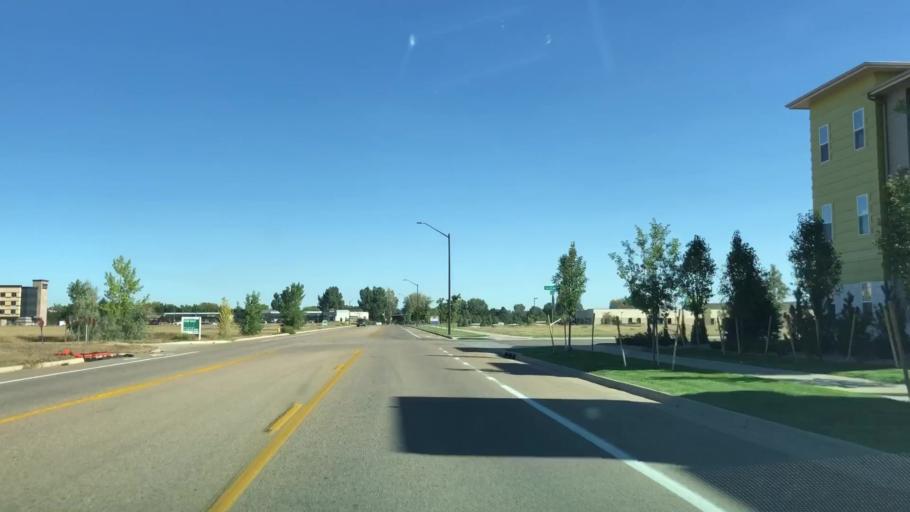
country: US
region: Colorado
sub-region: Larimer County
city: Fort Collins
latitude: 40.5188
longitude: -105.0108
